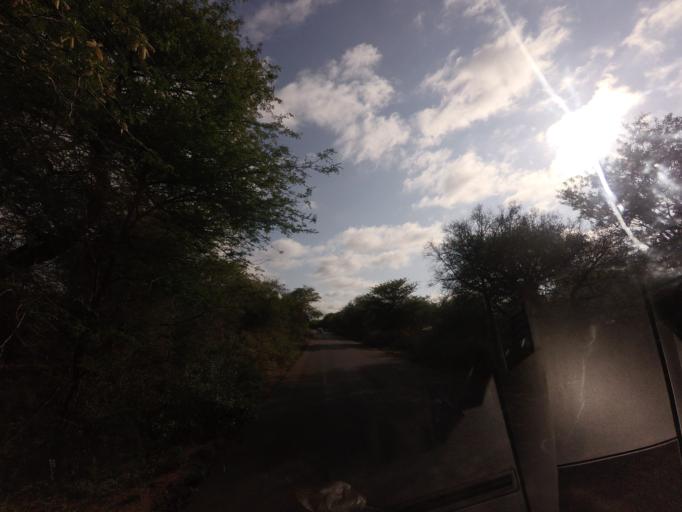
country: ZA
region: Mpumalanga
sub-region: Ehlanzeni District
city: Komatipoort
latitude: -25.2249
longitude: 31.8592
